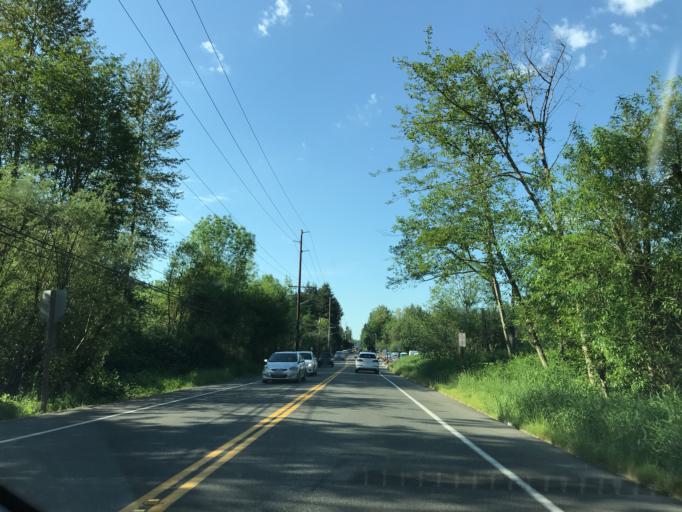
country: US
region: Washington
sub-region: King County
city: Issaquah
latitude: 47.4985
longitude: -122.0221
